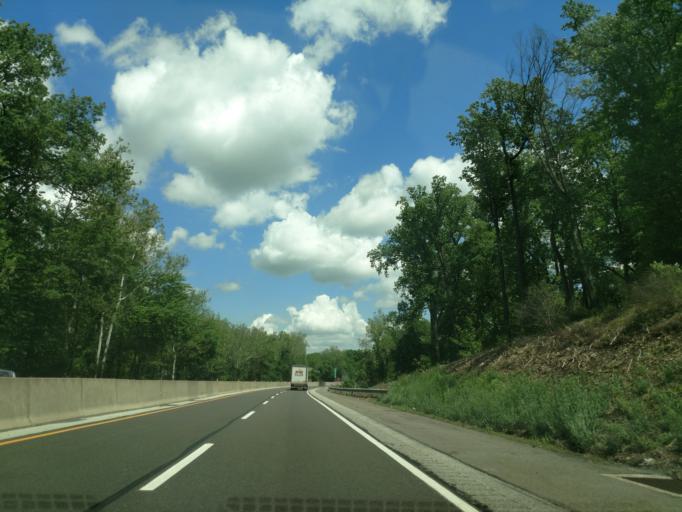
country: US
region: Pennsylvania
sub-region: Chester County
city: Chester Springs
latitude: 40.0652
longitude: -75.6402
